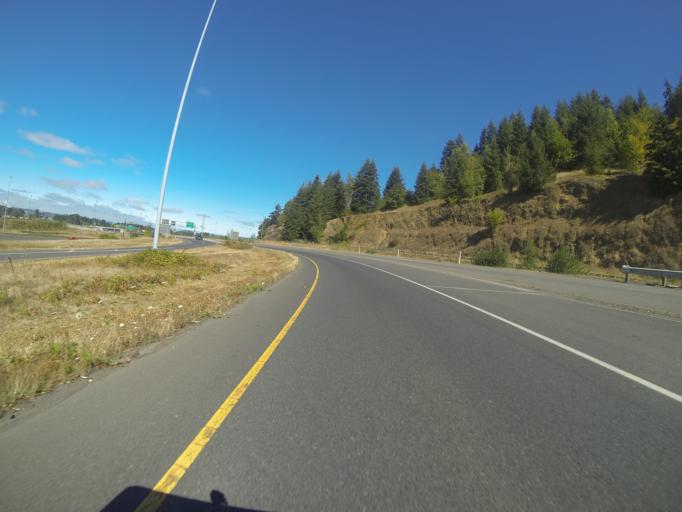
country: US
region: Washington
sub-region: Cowlitz County
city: Kelso
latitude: 46.1061
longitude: -122.8766
